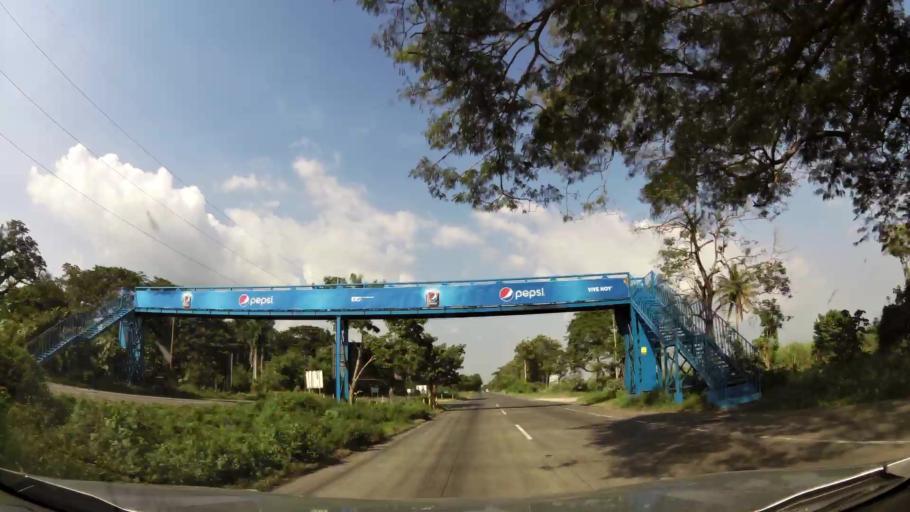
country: GT
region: Escuintla
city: Puerto San Jose
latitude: 14.0082
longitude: -90.7856
